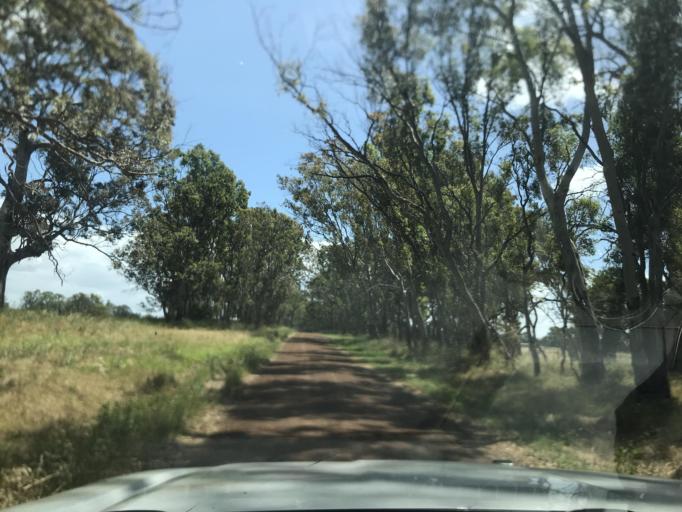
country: AU
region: South Australia
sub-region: Wattle Range
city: Penola
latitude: -37.2863
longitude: 141.4967
